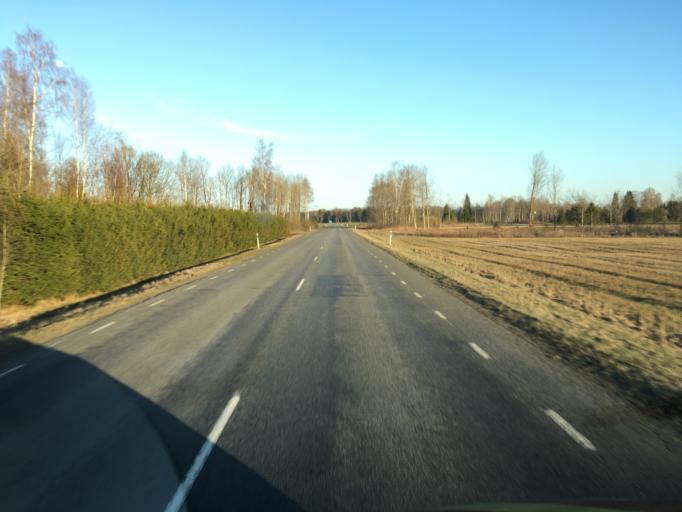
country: EE
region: Raplamaa
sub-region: Kehtna vald
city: Kehtna
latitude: 59.0605
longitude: 24.9377
